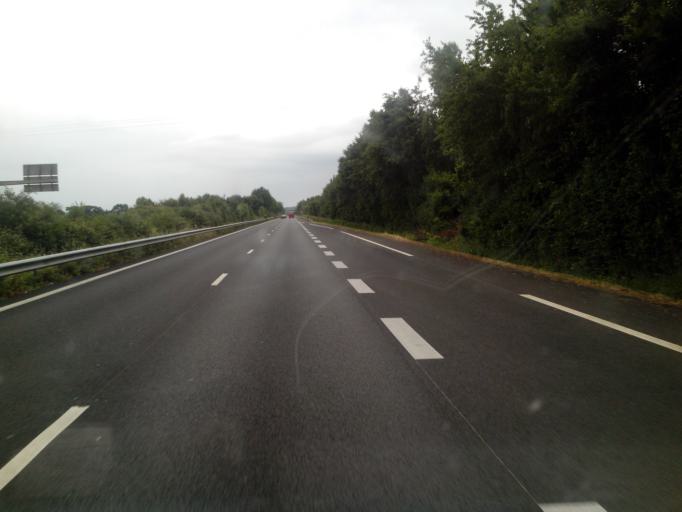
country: FR
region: Pays de la Loire
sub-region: Departement de la Loire-Atlantique
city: Jans
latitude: 47.6235
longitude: -1.6417
